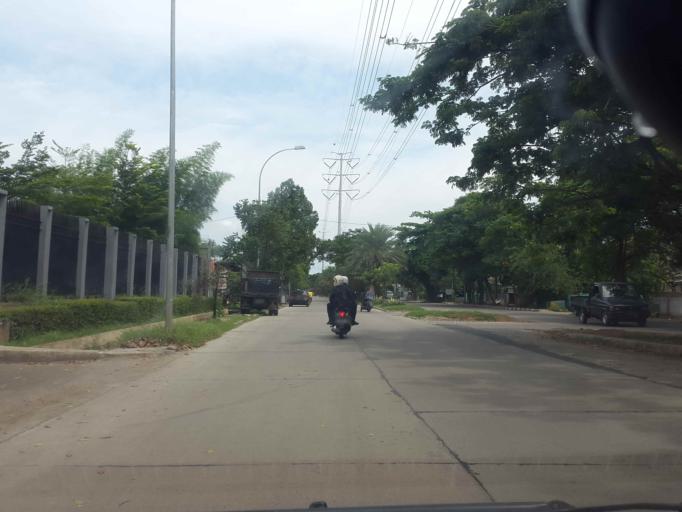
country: ID
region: Banten
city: Tangerang
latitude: -6.1547
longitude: 106.6445
